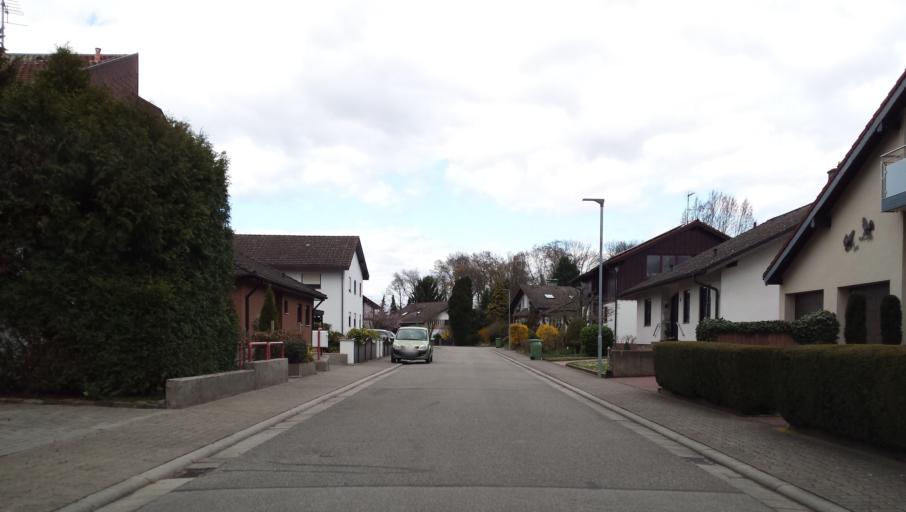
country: DE
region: Hesse
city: Zwingenberg
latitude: 49.7040
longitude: 8.5780
